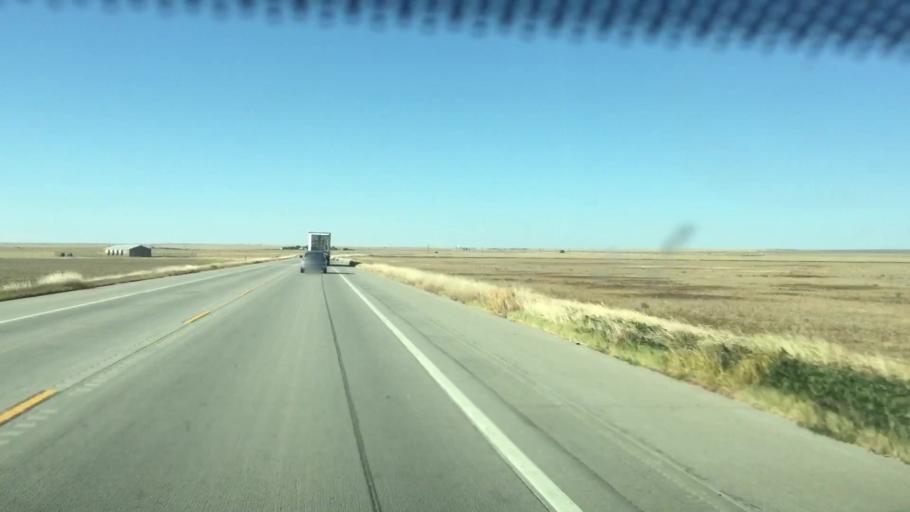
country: US
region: Colorado
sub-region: Kiowa County
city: Eads
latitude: 38.3696
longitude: -102.7264
